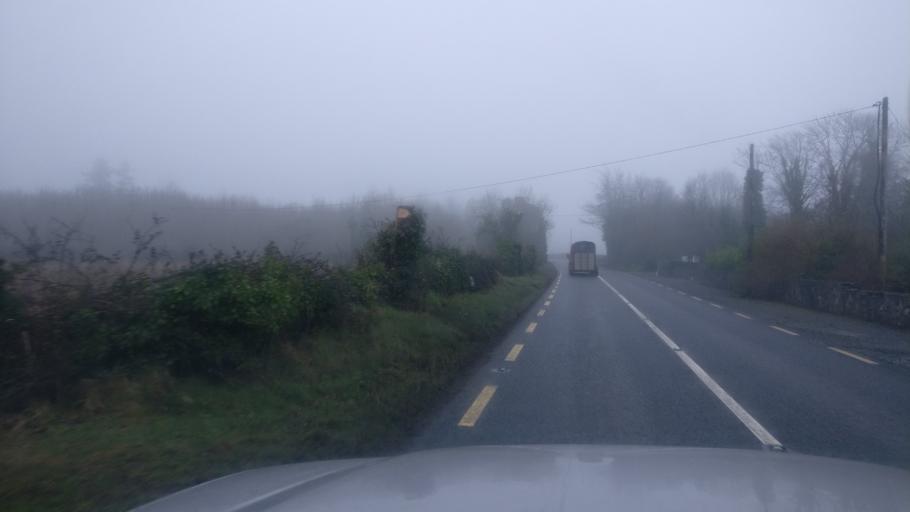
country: IE
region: Connaught
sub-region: County Galway
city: Gort
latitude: 53.1426
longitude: -8.7009
